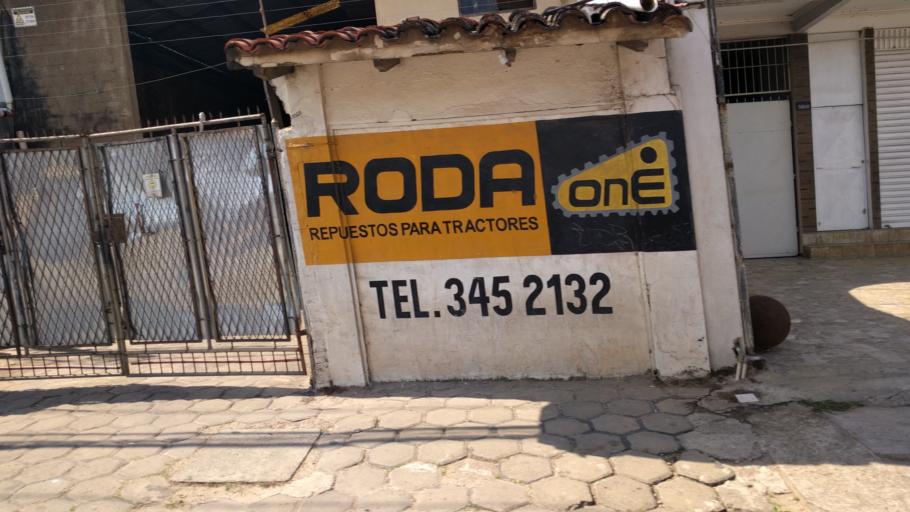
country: BO
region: Santa Cruz
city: Santa Cruz de la Sierra
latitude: -17.7396
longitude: -63.1711
